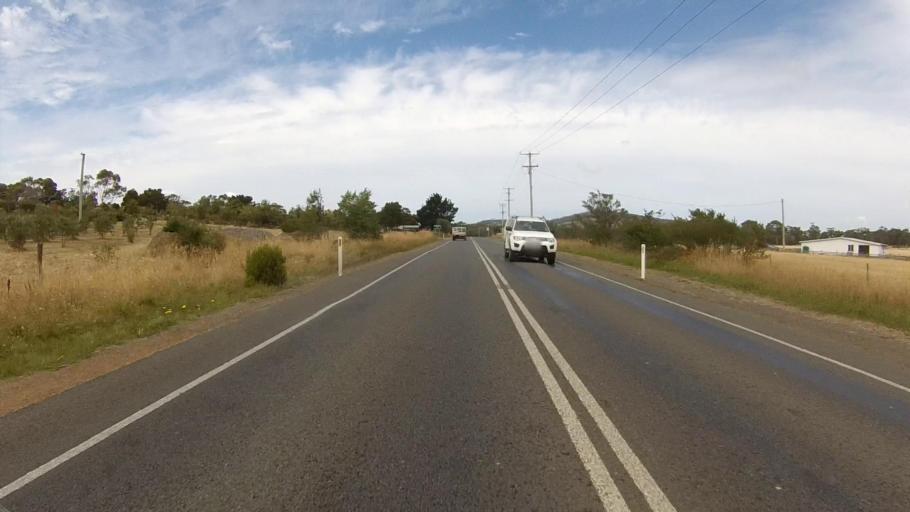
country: AU
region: Tasmania
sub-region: Clarence
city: Sandford
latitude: -42.9321
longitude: 147.4913
